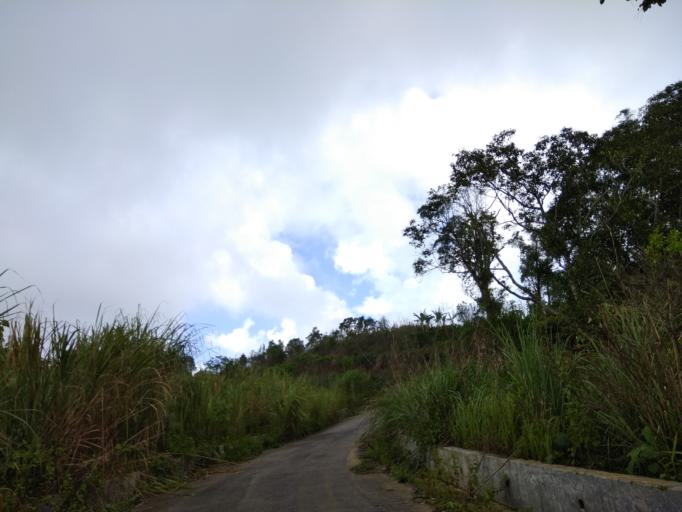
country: BD
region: Chittagong
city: Bandarban
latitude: 21.7382
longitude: 92.4205
